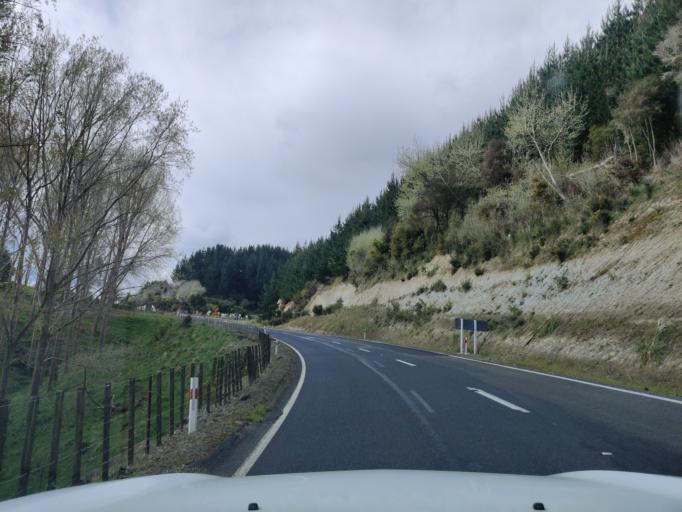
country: NZ
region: Manawatu-Wanganui
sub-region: Wanganui District
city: Wanganui
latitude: -39.8000
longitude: 175.1965
